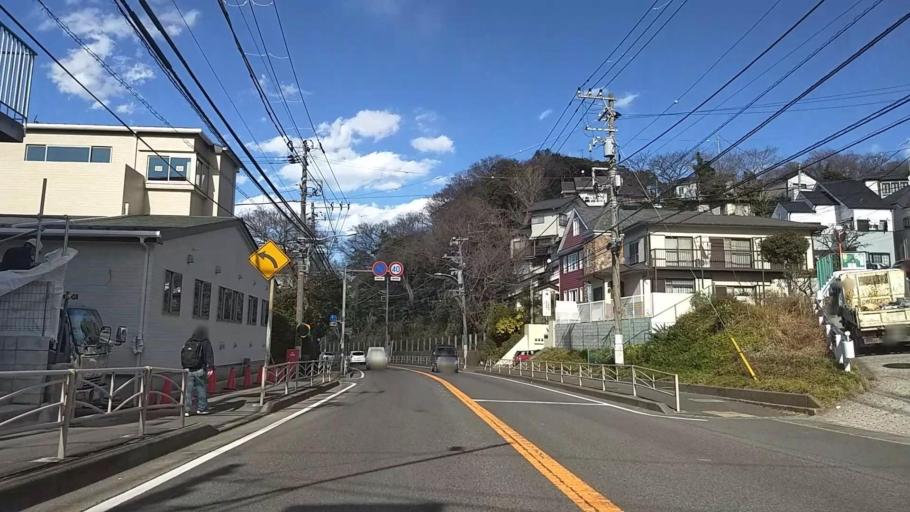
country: JP
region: Kanagawa
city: Yokohama
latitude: 35.3637
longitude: 139.6305
